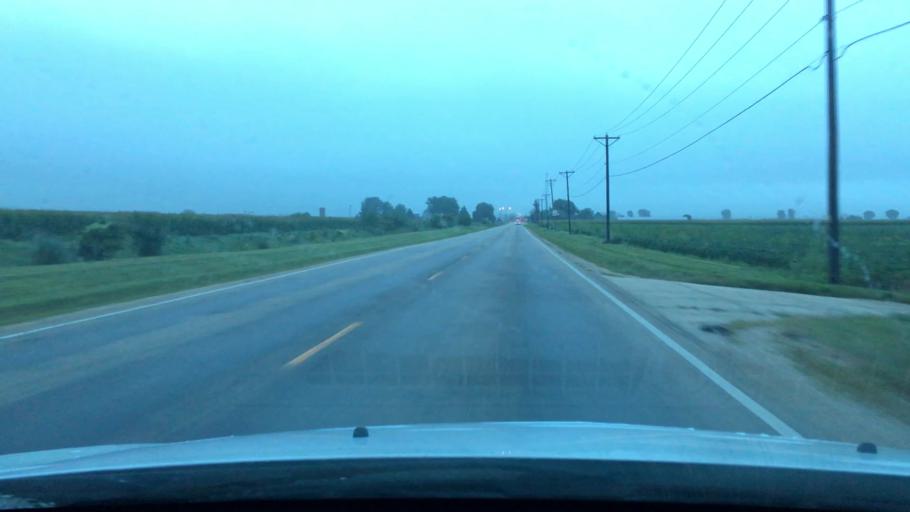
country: US
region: Illinois
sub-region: Ogle County
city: Rochelle
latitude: 41.9232
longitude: -89.0442
